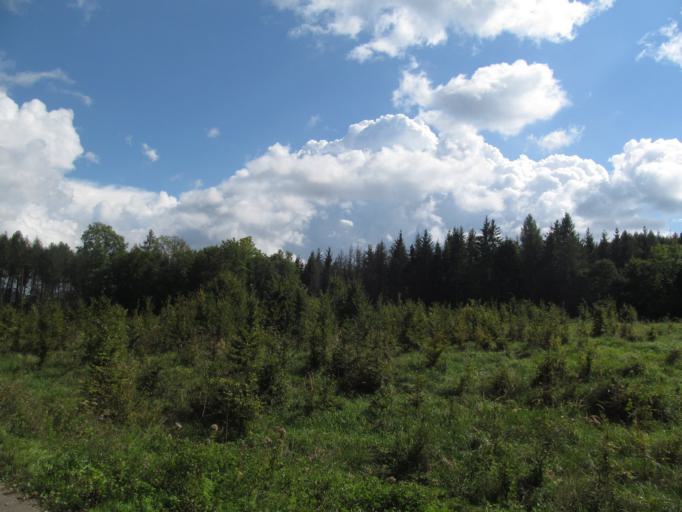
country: HU
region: Borsod-Abauj-Zemplen
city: Kazincbarcika
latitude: 48.1042
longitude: 20.5702
